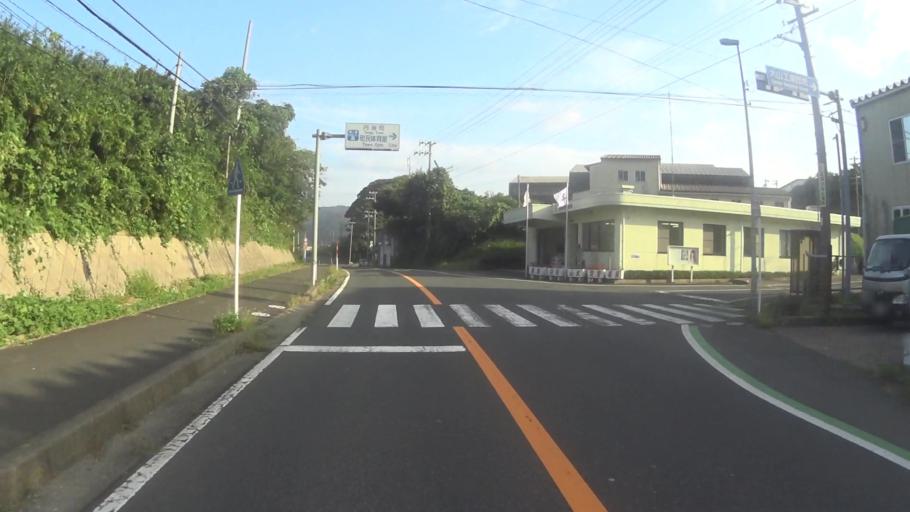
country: JP
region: Kyoto
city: Miyazu
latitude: 35.7222
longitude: 135.1020
